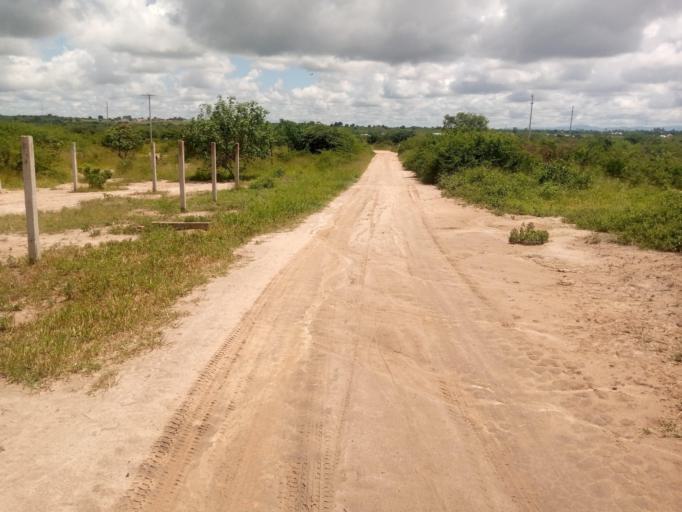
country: TZ
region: Dodoma
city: Dodoma
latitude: -6.1128
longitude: 35.7391
